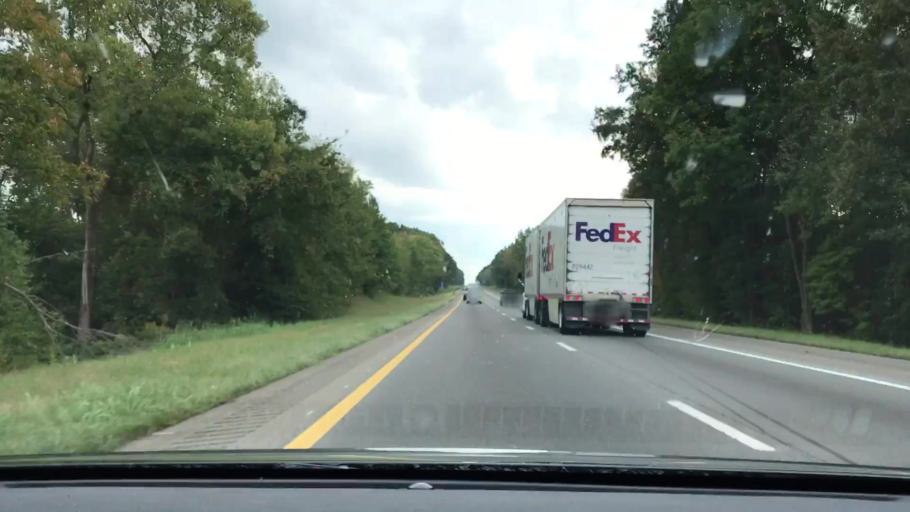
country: US
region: Tennessee
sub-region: Cheatham County
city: Pleasant View
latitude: 36.4256
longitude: -87.0629
